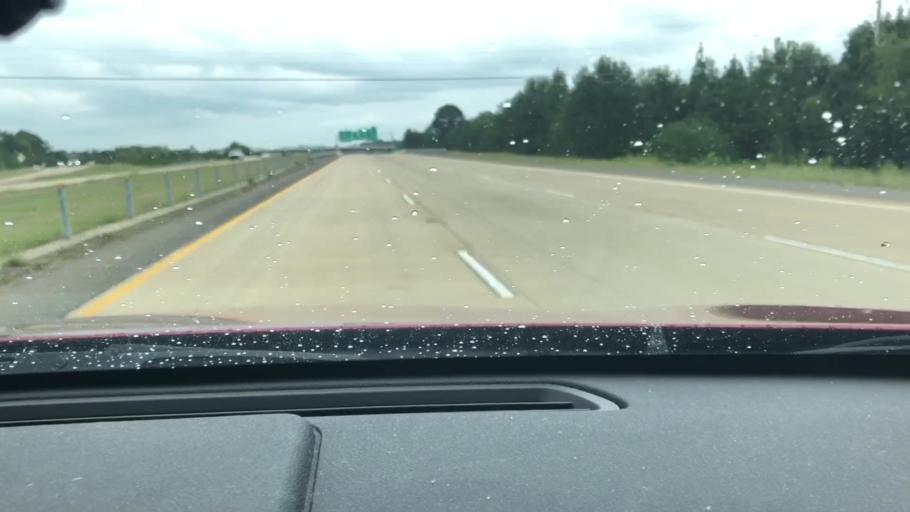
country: US
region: Texas
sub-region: Bowie County
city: Texarkana
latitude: 33.3853
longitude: -94.0289
